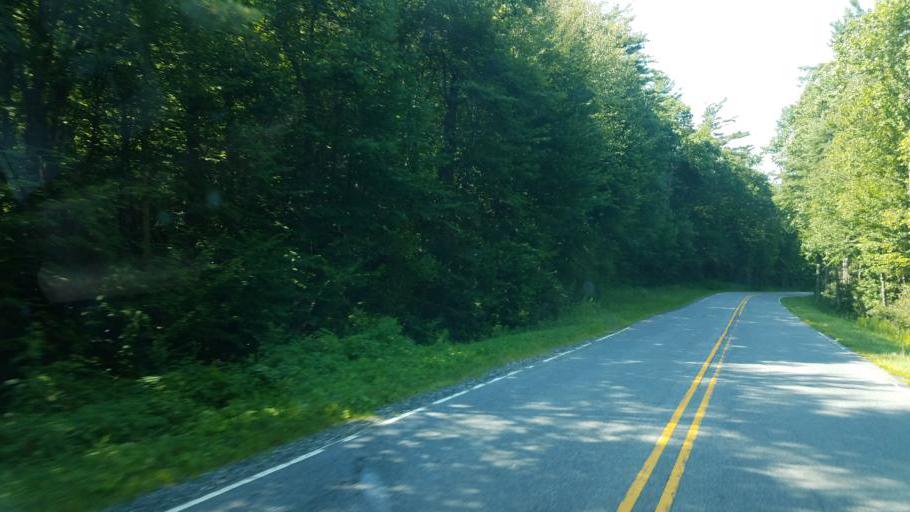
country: US
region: North Carolina
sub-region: Avery County
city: Newland
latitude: 35.9875
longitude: -81.8929
